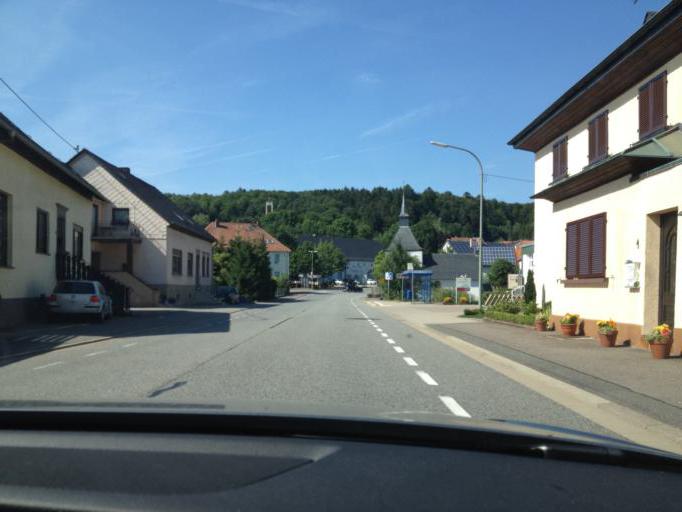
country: DE
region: Saarland
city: Tholey
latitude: 49.5361
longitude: 7.0390
